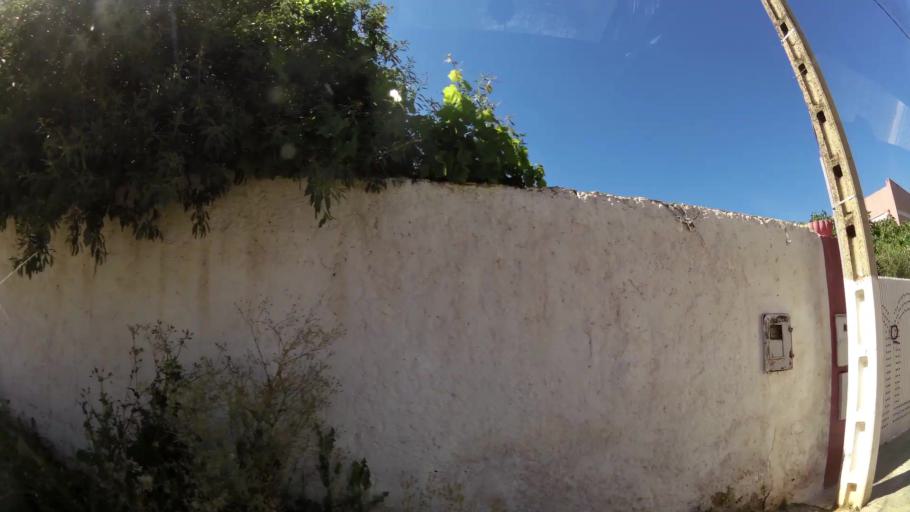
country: MA
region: Fes-Boulemane
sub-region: Fes
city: Fes
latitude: 34.0198
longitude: -4.9913
